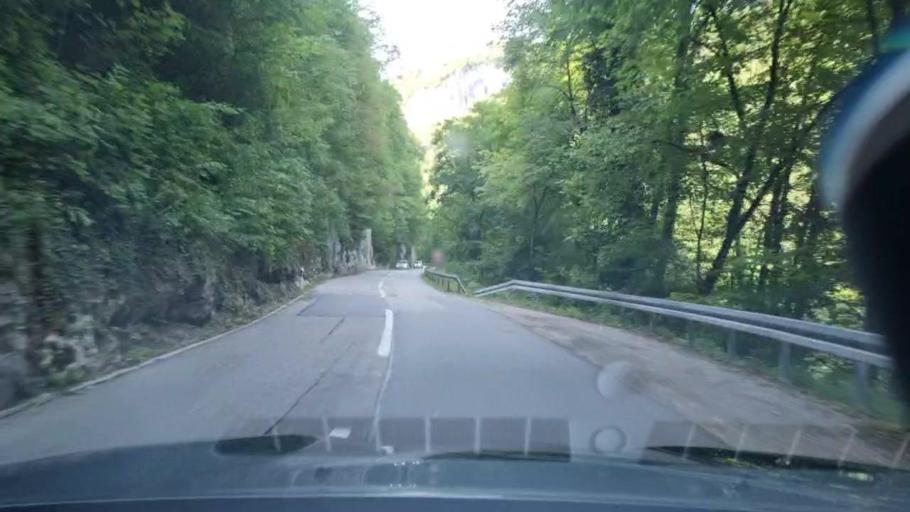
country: BA
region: Federation of Bosnia and Herzegovina
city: Bosanska Krupa
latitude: 44.8687
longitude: 16.0876
